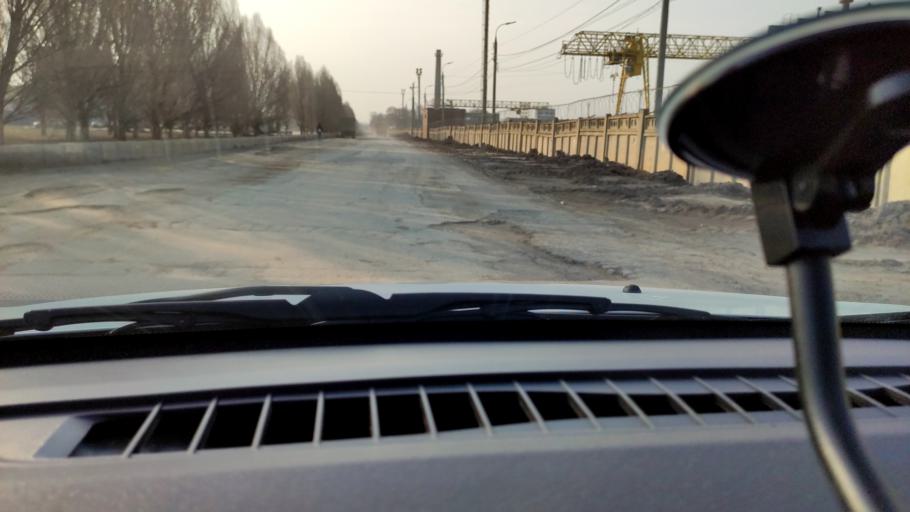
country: RU
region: Samara
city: Samara
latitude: 53.1852
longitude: 50.2599
